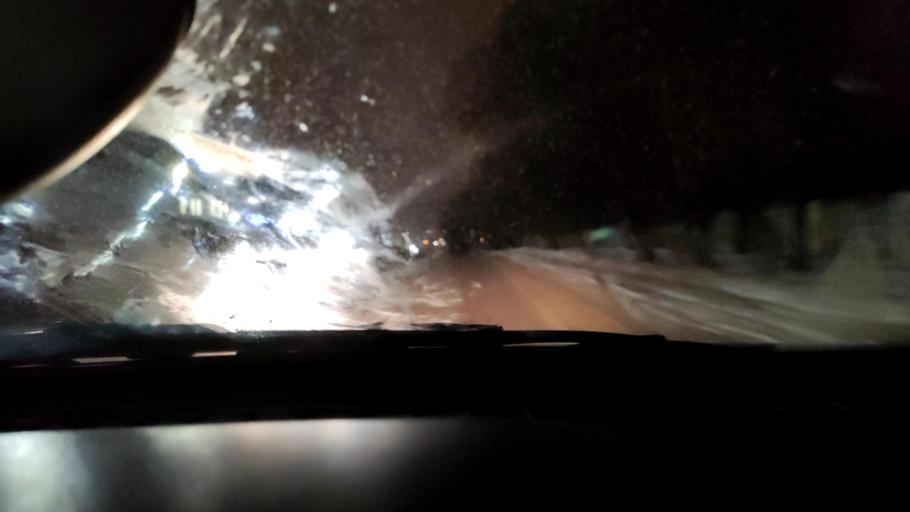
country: RU
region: Perm
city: Kultayevo
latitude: 57.9866
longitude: 55.9363
